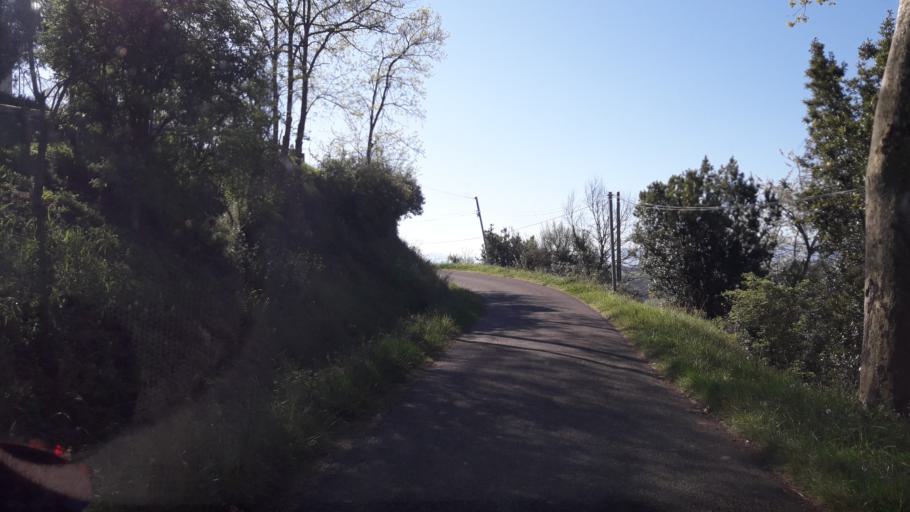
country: FR
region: Midi-Pyrenees
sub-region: Departement de la Haute-Garonne
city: Montesquieu-Volvestre
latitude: 43.2006
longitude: 1.2799
